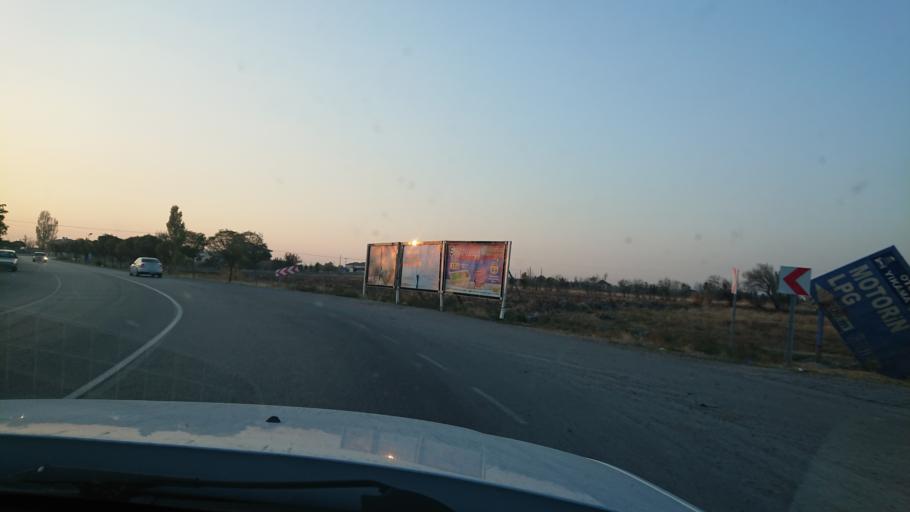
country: TR
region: Aksaray
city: Aksaray
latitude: 38.3097
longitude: 34.0660
